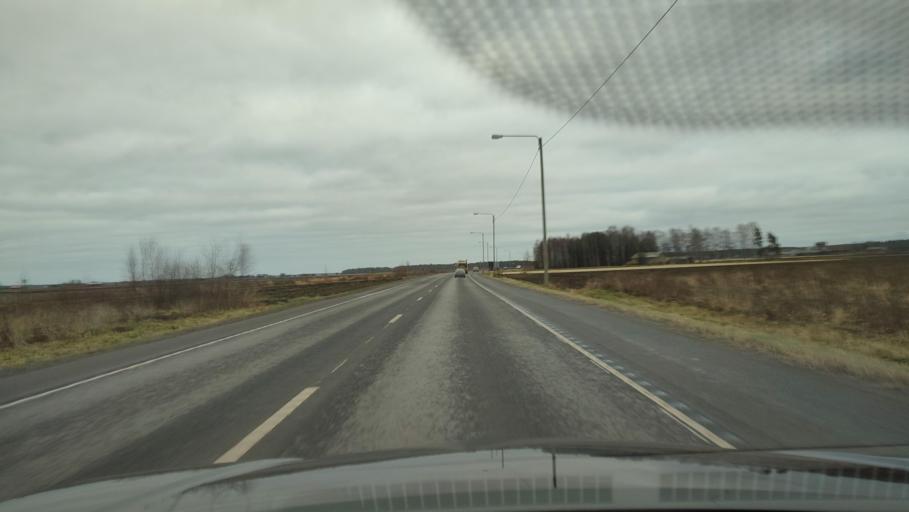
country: FI
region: Southern Ostrobothnia
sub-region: Seinaejoki
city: Ilmajoki
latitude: 62.7360
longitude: 22.6085
